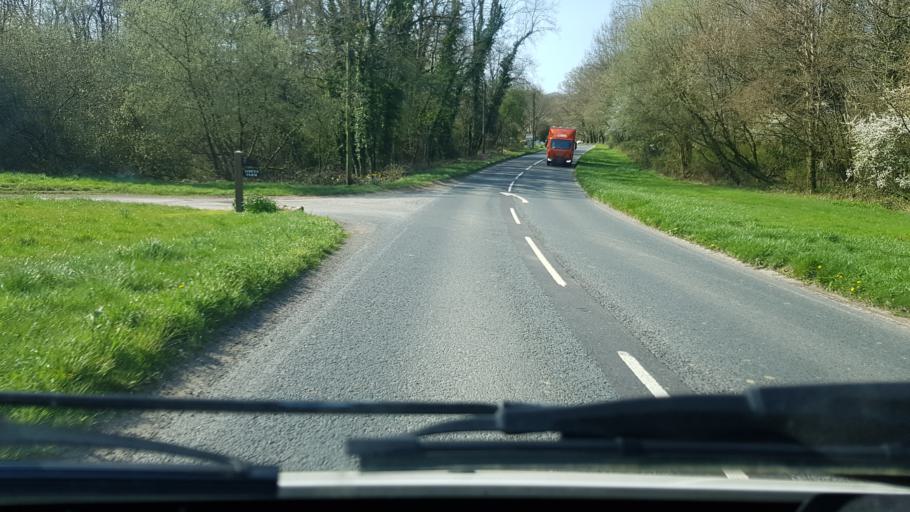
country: GB
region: England
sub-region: West Sussex
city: Fernhurst
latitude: 51.0317
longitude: -0.7296
